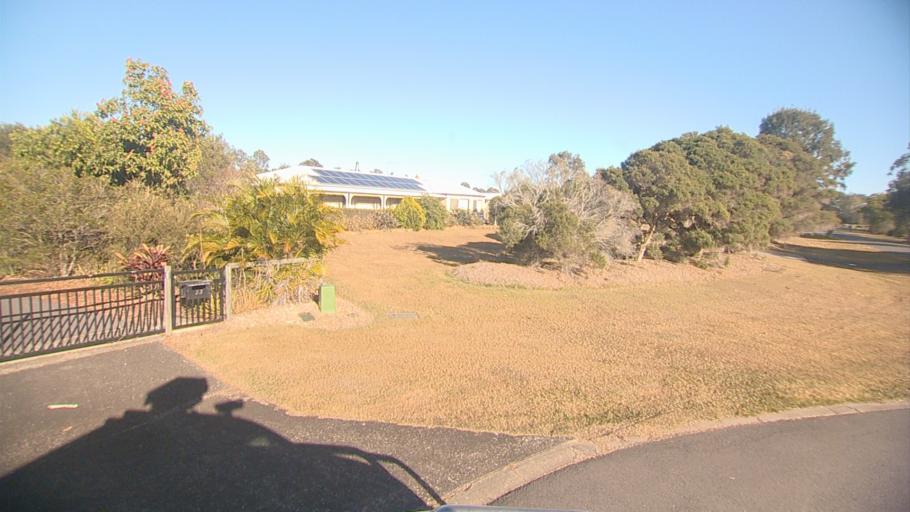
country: AU
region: Queensland
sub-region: Logan
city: North Maclean
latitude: -27.8271
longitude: 153.0091
